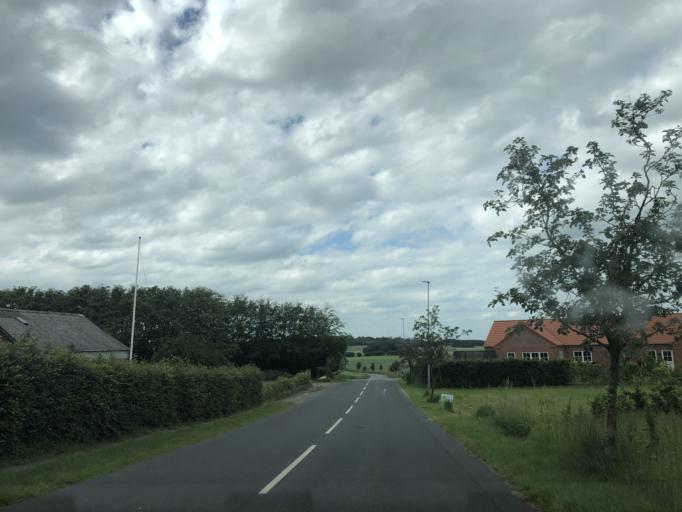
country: DK
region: Central Jutland
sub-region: Skanderborg Kommune
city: Ry
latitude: 56.1807
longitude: 9.7734
